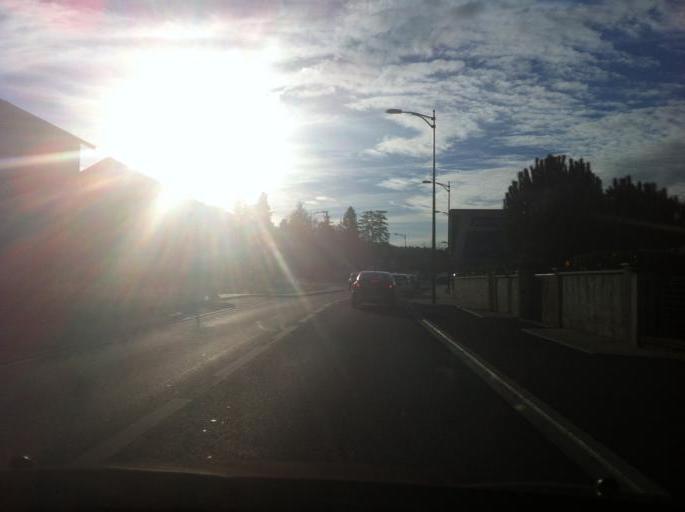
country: FR
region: Aquitaine
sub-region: Departement de la Dordogne
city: Chancelade
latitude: 45.1865
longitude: 0.6663
